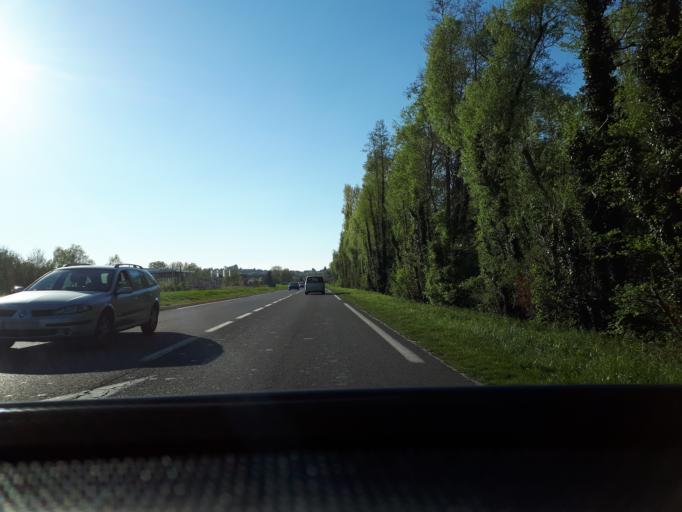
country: FR
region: Rhone-Alpes
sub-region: Departement de l'Isere
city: Domarin
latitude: 45.5916
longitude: 5.2531
